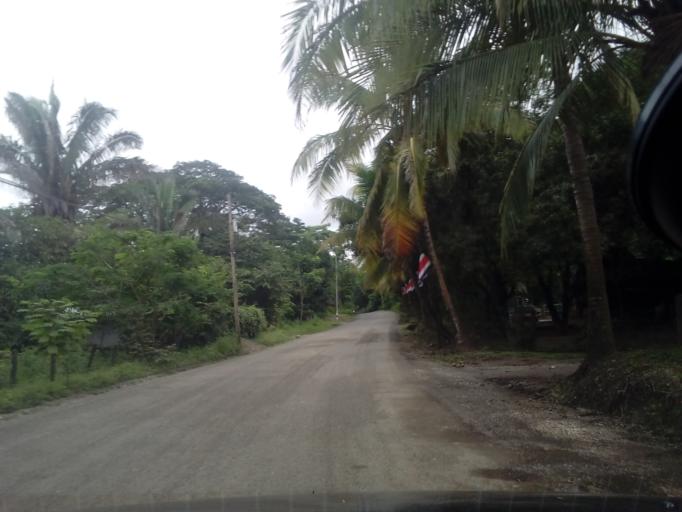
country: CR
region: Guanacaste
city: Samara
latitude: 9.9168
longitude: -85.5508
